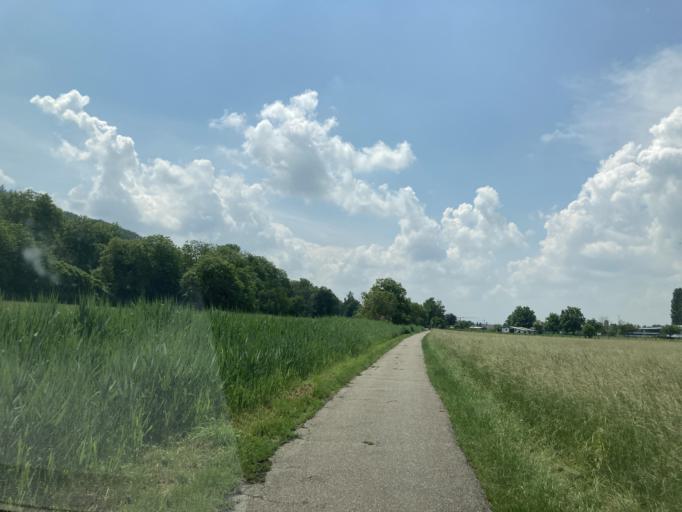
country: DE
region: Baden-Wuerttemberg
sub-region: Karlsruhe Region
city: Weingarten
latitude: 49.0644
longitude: 8.5363
